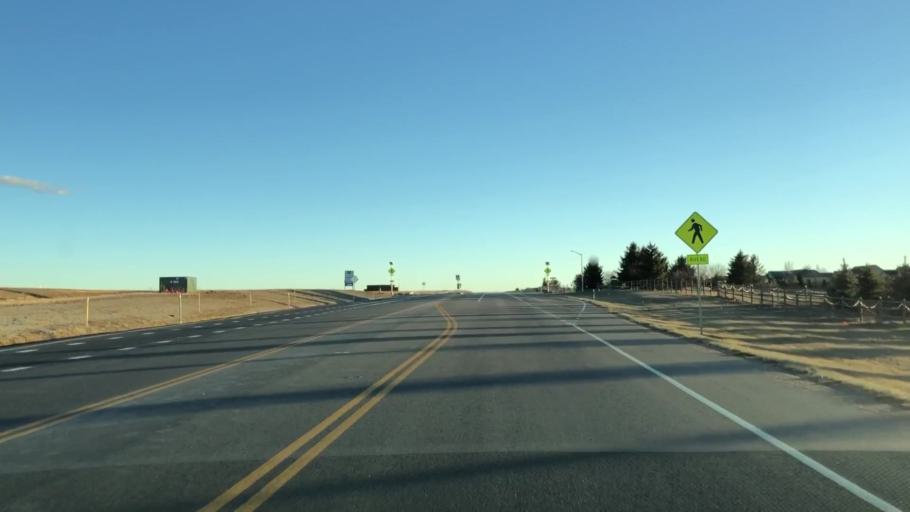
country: US
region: Colorado
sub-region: Weld County
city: Windsor
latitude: 40.4472
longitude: -104.9441
